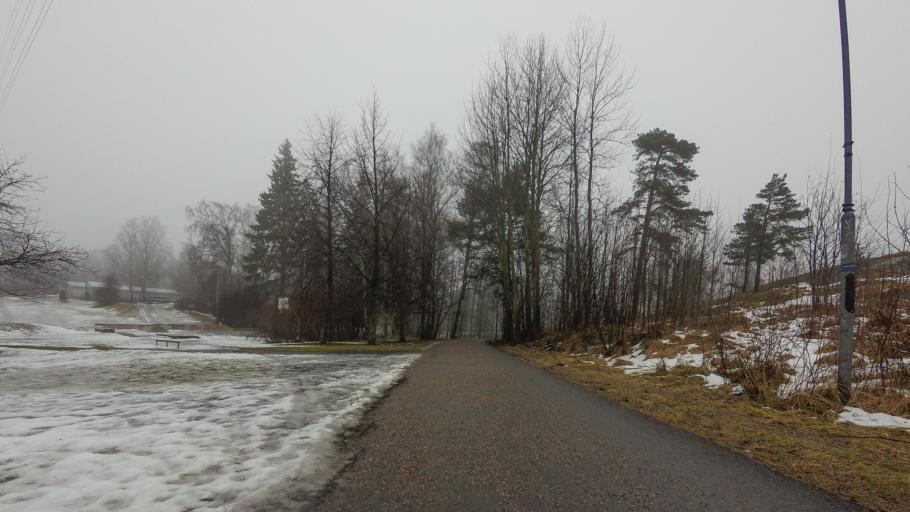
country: FI
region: Uusimaa
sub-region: Helsinki
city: Vantaa
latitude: 60.2093
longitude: 25.0449
